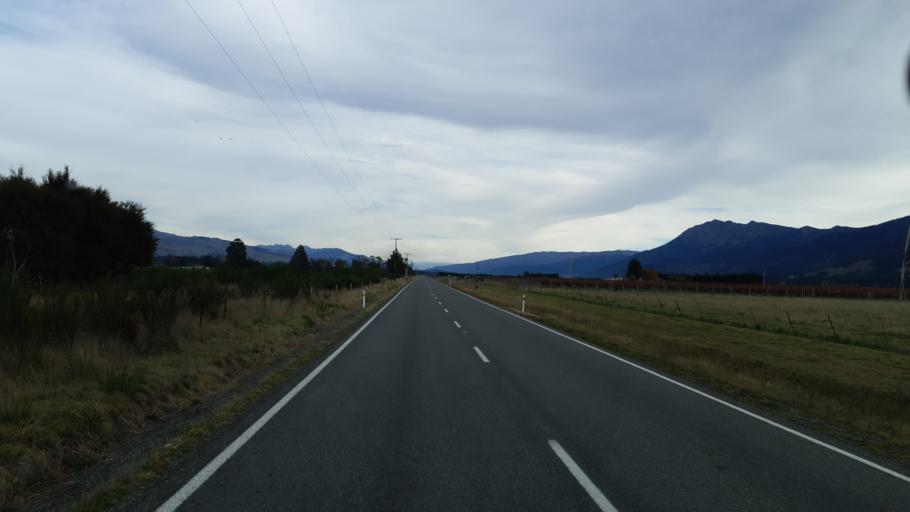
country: NZ
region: Tasman
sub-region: Tasman District
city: Richmond
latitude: -41.6059
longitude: 173.4096
